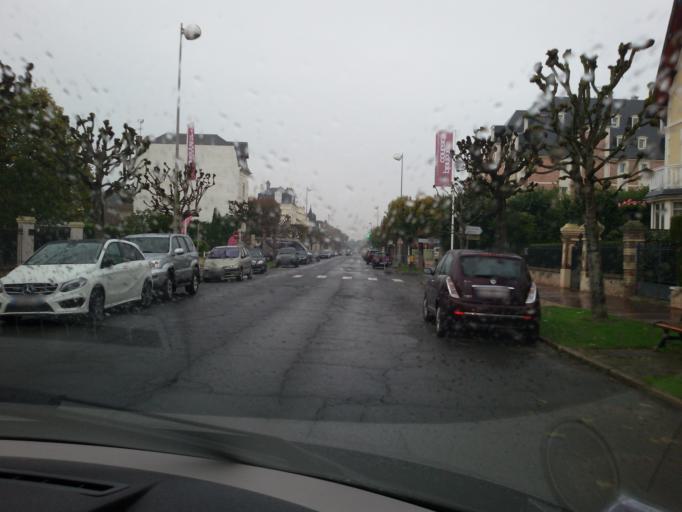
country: FR
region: Lower Normandy
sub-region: Departement du Calvados
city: Deauville
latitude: 49.3577
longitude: 0.0747
